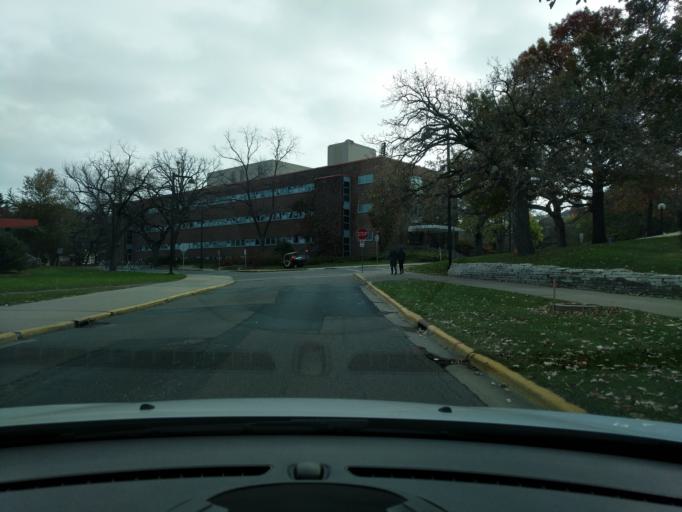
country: US
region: Minnesota
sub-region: Hennepin County
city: Minneapolis
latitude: 44.9792
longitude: -93.2383
